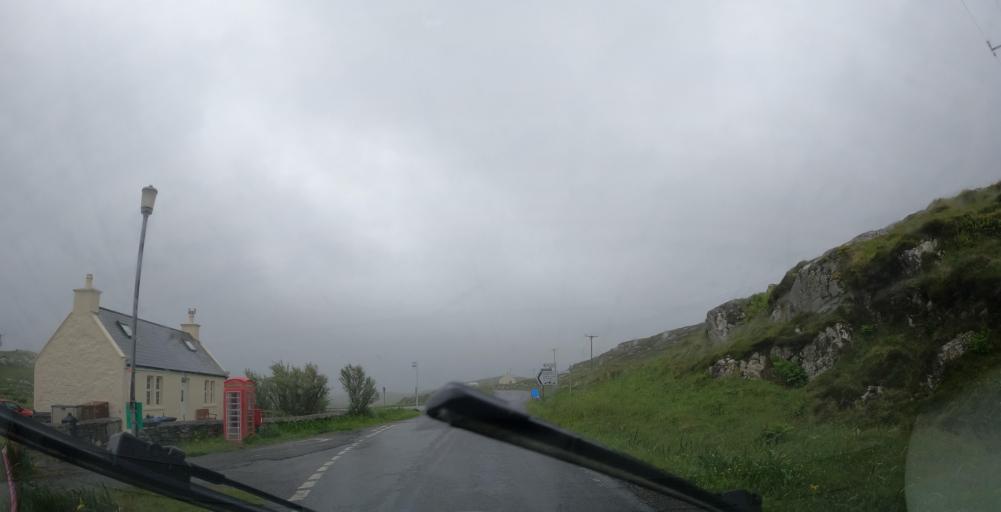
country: GB
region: Scotland
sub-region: Eilean Siar
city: Barra
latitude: 57.0134
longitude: -7.4306
